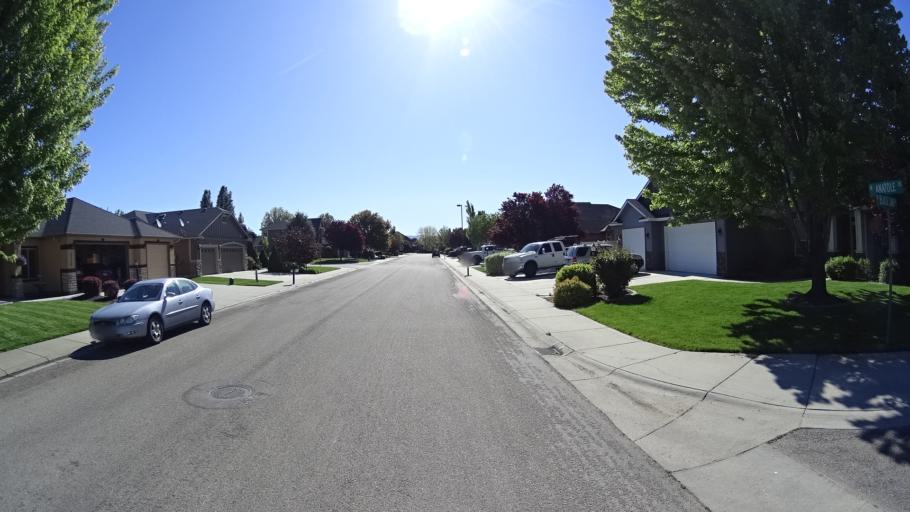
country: US
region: Idaho
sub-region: Ada County
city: Meridian
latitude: 43.6552
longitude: -116.4281
